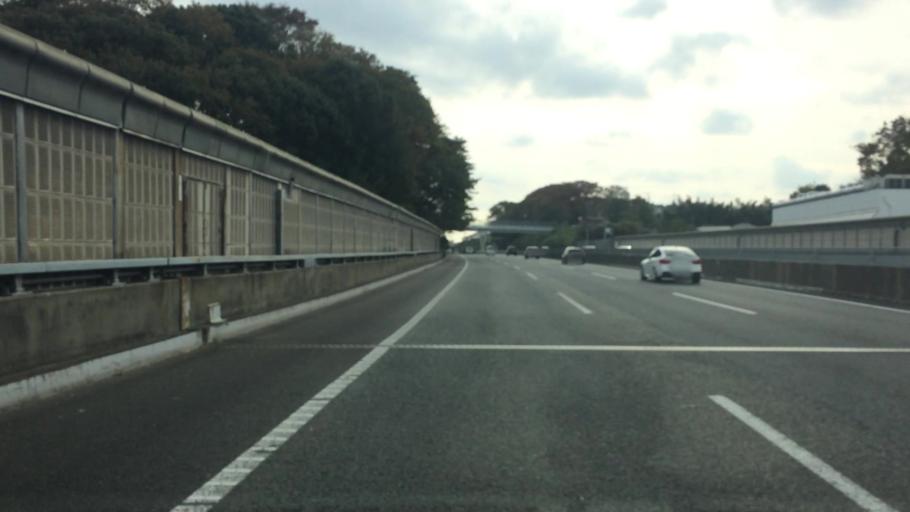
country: JP
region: Tokyo
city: Chofugaoka
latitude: 35.5835
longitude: 139.6191
